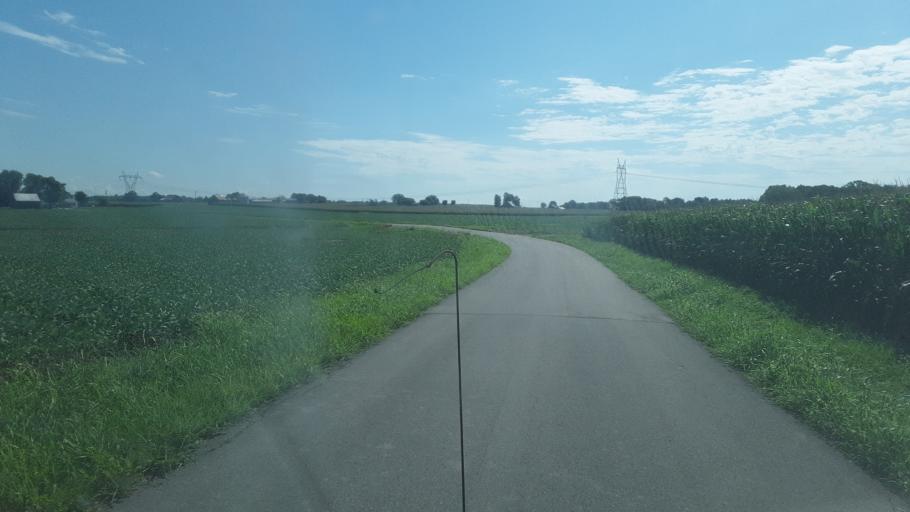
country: US
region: Kentucky
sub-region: Todd County
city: Elkton
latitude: 36.7841
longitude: -87.2237
